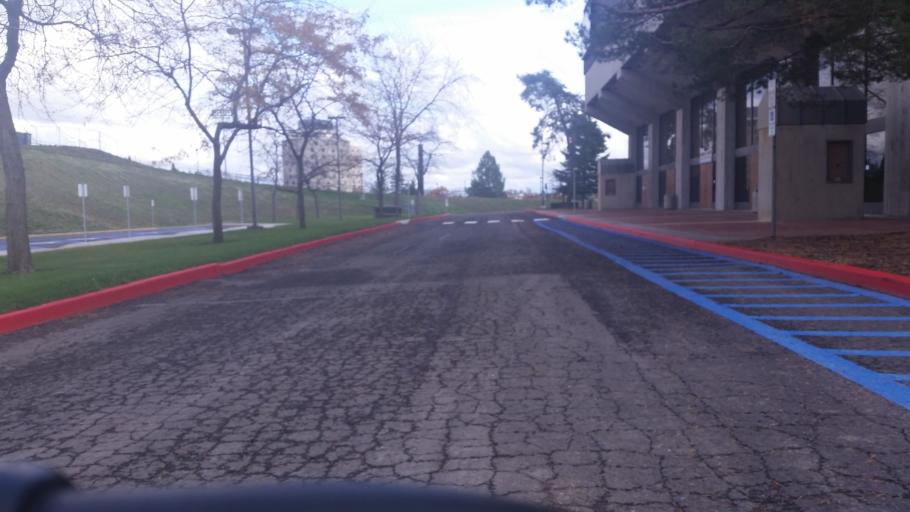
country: US
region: Washington
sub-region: Spokane County
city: Cheney
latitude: 47.4918
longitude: -117.5900
